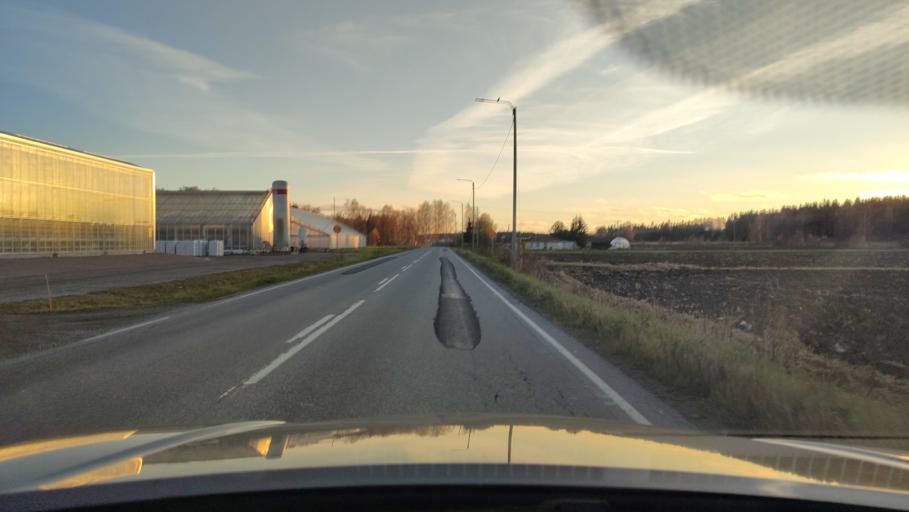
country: FI
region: Ostrobothnia
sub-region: Sydosterbotten
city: Naerpes
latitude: 62.4343
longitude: 21.3496
